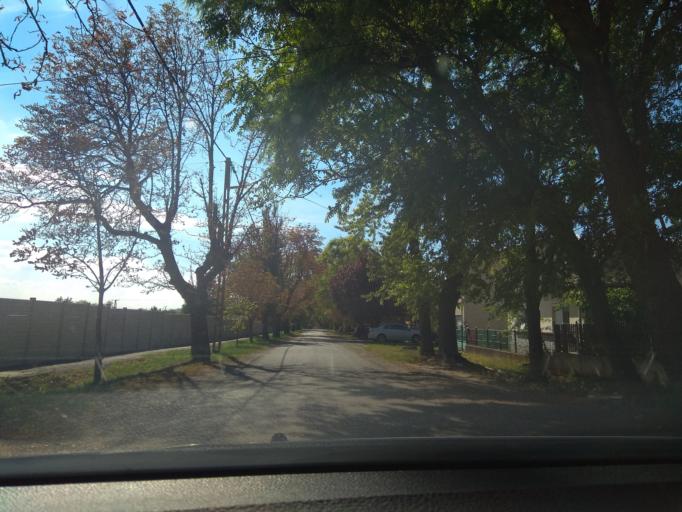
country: HU
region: Borsod-Abauj-Zemplen
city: Tallya
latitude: 48.2319
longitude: 21.2277
